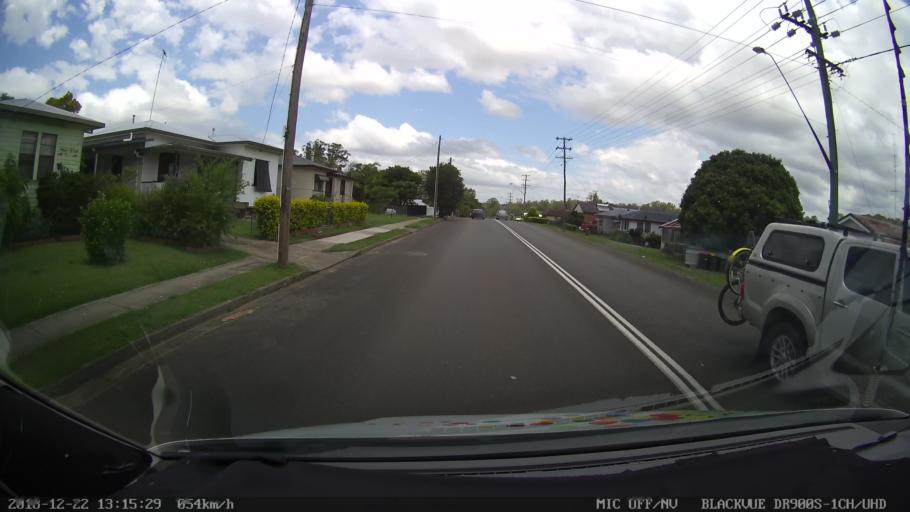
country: AU
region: New South Wales
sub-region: Clarence Valley
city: South Grafton
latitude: -29.7183
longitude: 152.9389
